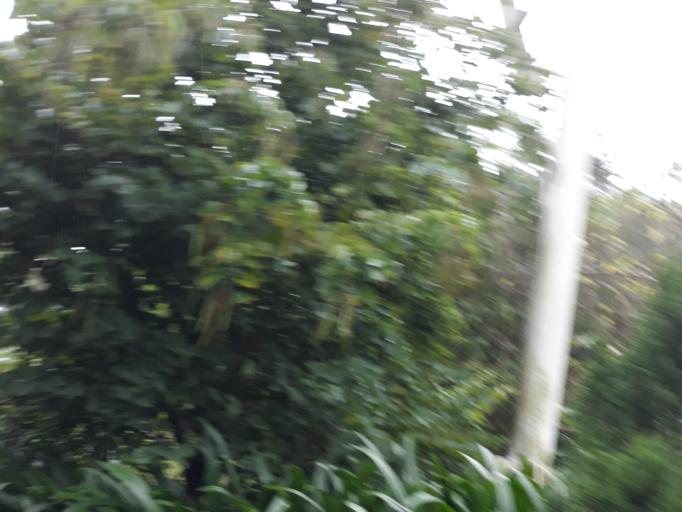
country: TW
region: Taipei
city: Taipei
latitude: 24.9953
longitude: 121.5853
